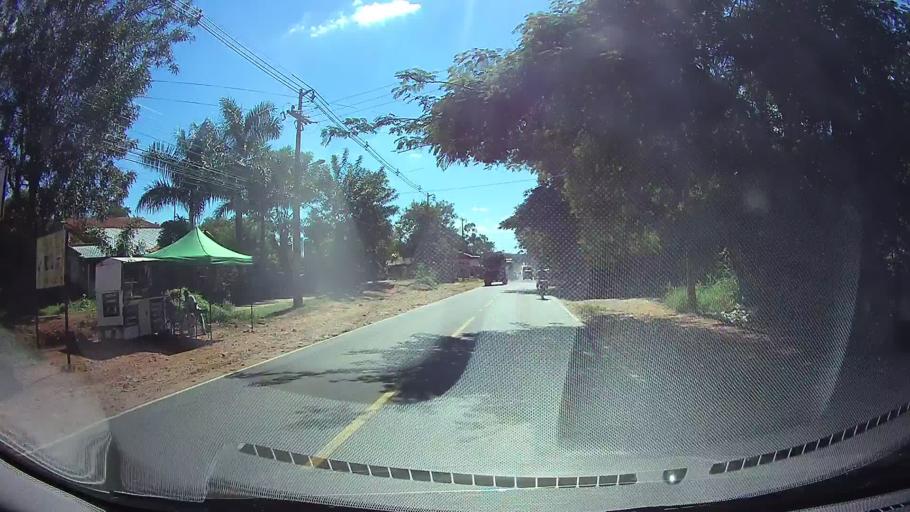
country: PY
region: Central
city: Limpio
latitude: -25.2332
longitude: -57.4755
